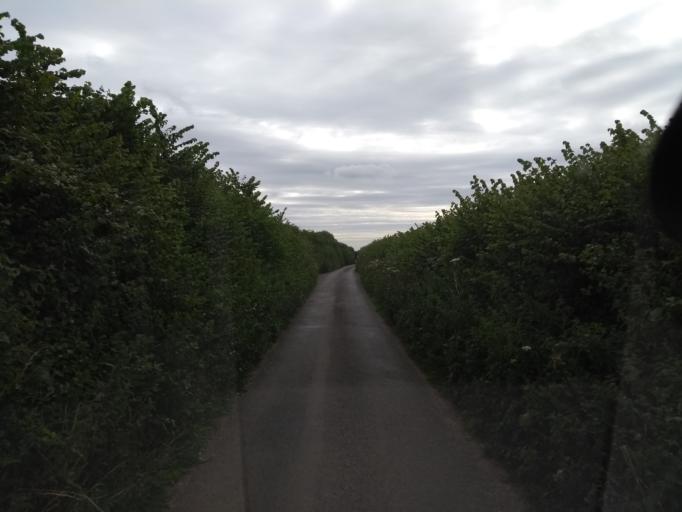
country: GB
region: England
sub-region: Somerset
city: Bishops Lydeard
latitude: 51.0409
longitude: -3.2345
